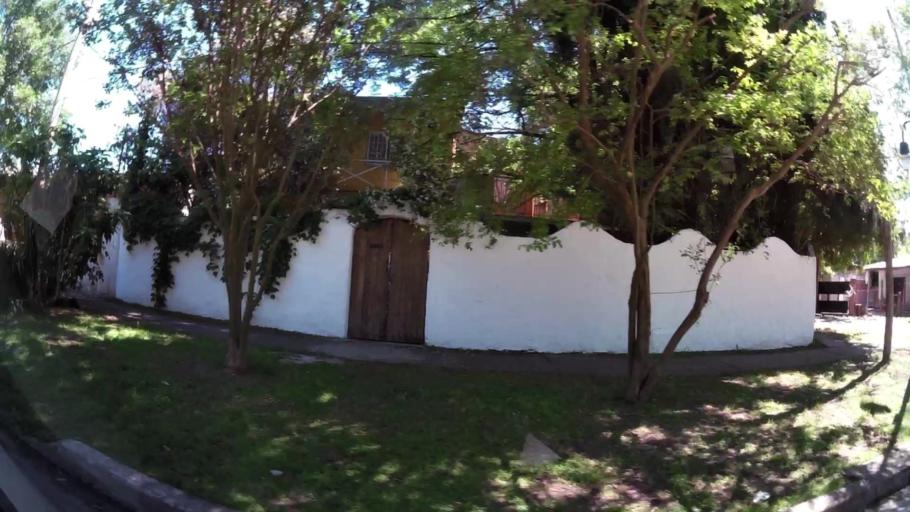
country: AR
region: Buenos Aires
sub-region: Partido de Tigre
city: Tigre
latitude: -34.5044
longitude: -58.6114
